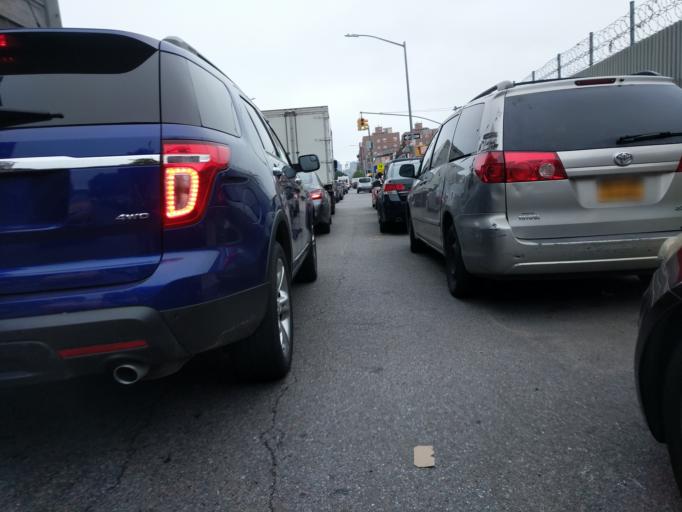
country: US
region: New York
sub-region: Kings County
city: Brooklyn
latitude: 40.6972
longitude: -73.9535
